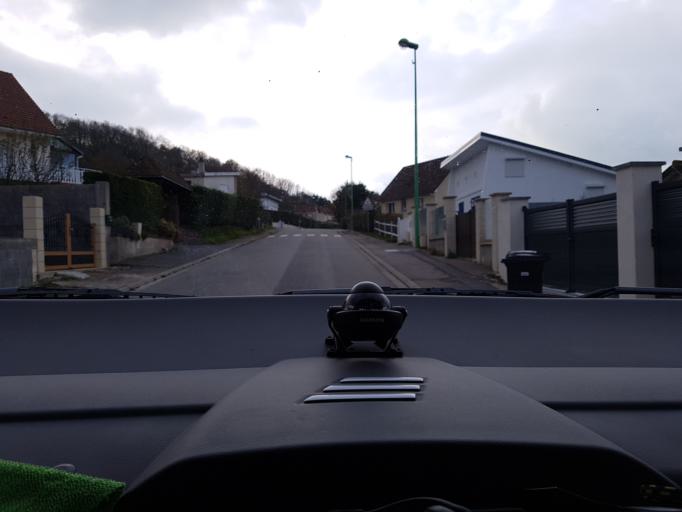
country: FR
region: Haute-Normandie
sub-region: Departement de la Seine-Maritime
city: Berneval-le-Grand
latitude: 49.9670
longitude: 1.2035
